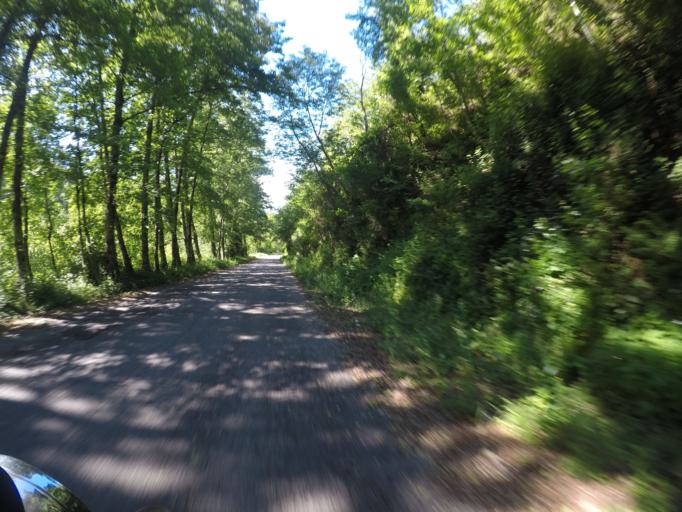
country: IT
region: Tuscany
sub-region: Provincia di Massa-Carrara
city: Fosdinovo
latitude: 44.1447
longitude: 10.0848
